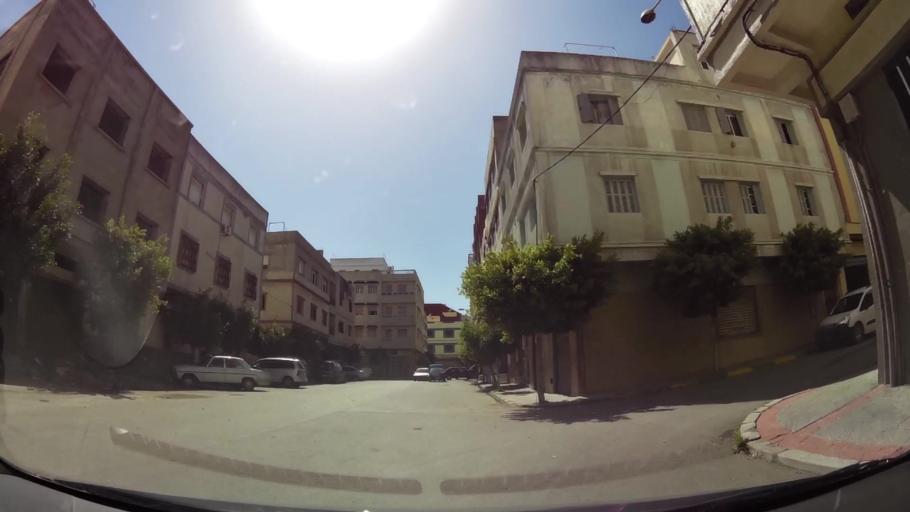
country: MA
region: Tanger-Tetouan
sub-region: Tanger-Assilah
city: Tangier
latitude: 35.7498
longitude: -5.8106
